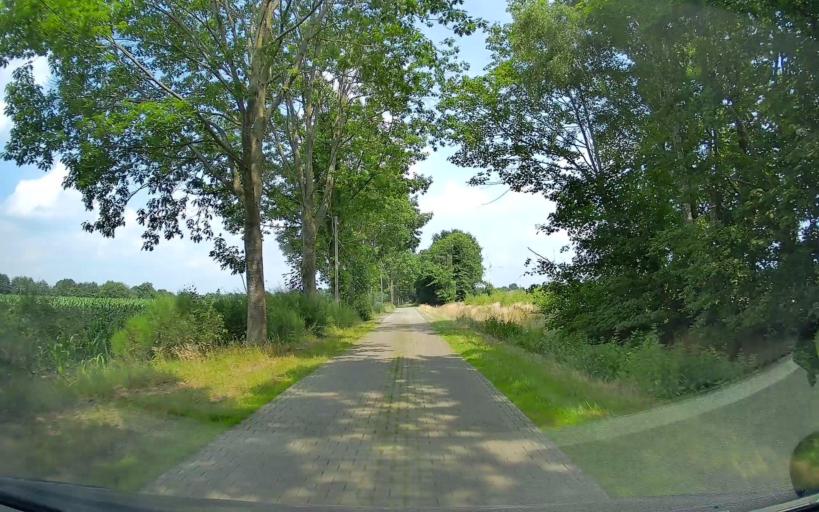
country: DE
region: Lower Saxony
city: Bosel
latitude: 53.0058
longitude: 7.9066
